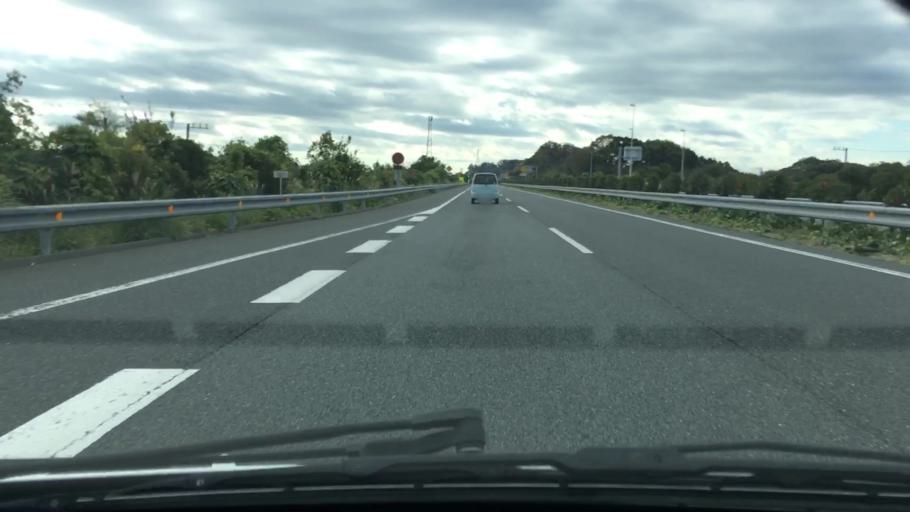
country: JP
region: Chiba
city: Kimitsu
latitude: 35.2505
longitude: 139.8918
